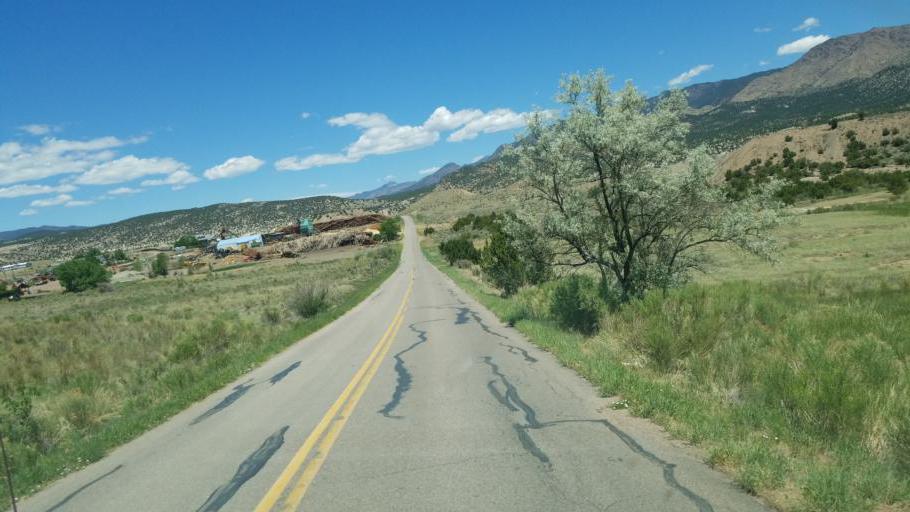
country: US
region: Colorado
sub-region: Fremont County
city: Canon City
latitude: 38.4839
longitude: -105.2086
